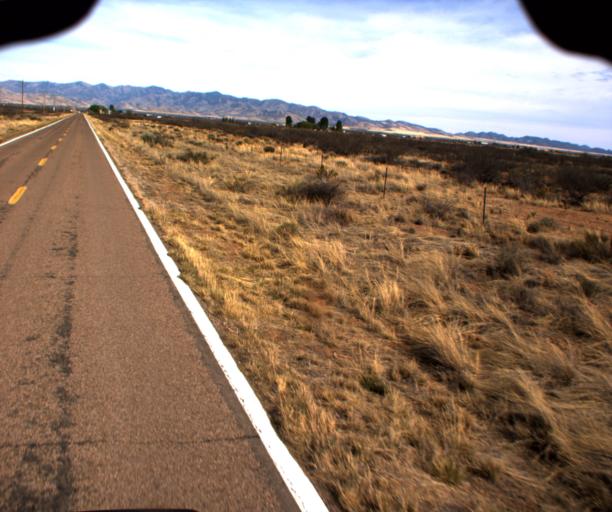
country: US
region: Arizona
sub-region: Cochise County
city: Willcox
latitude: 31.8761
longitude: -109.5836
